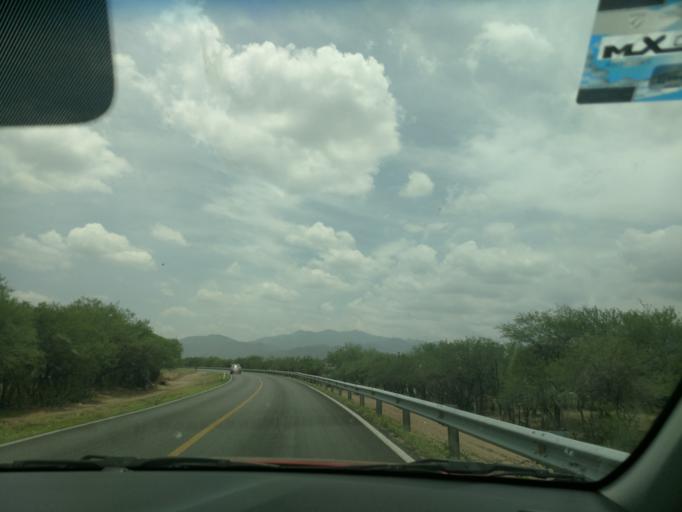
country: MX
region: San Luis Potosi
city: Zaragoza
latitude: 22.0202
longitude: -100.4015
